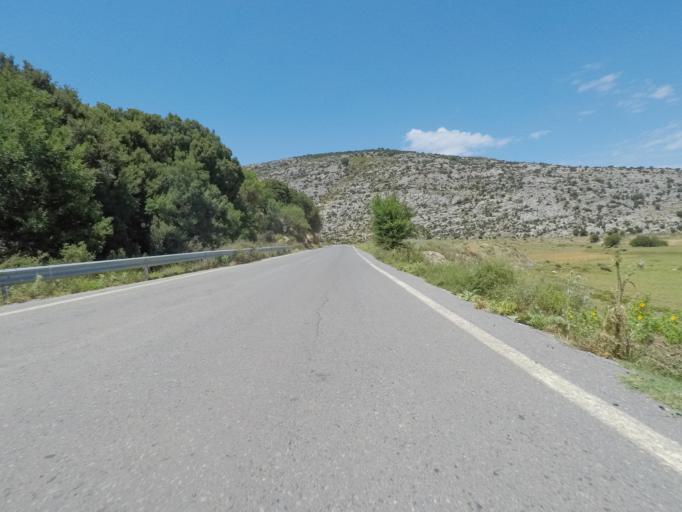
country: GR
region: Crete
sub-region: Nomos Irakleiou
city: Mokhos
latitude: 35.1907
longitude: 25.4322
